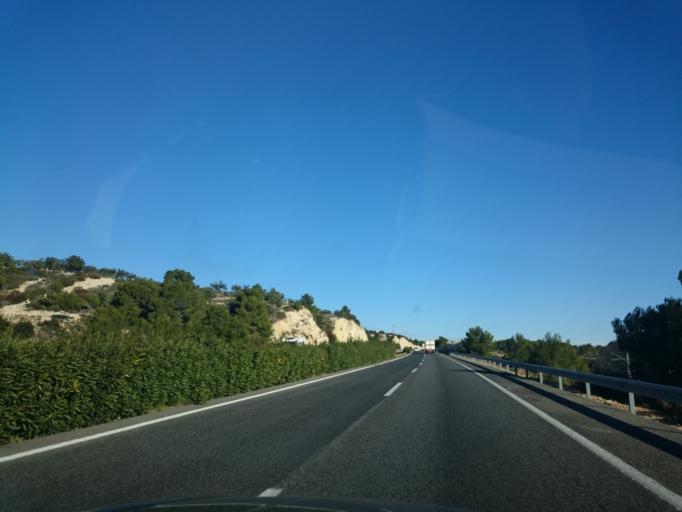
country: ES
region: Catalonia
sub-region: Provincia de Tarragona
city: L'Ampolla
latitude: 40.8362
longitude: 0.7424
